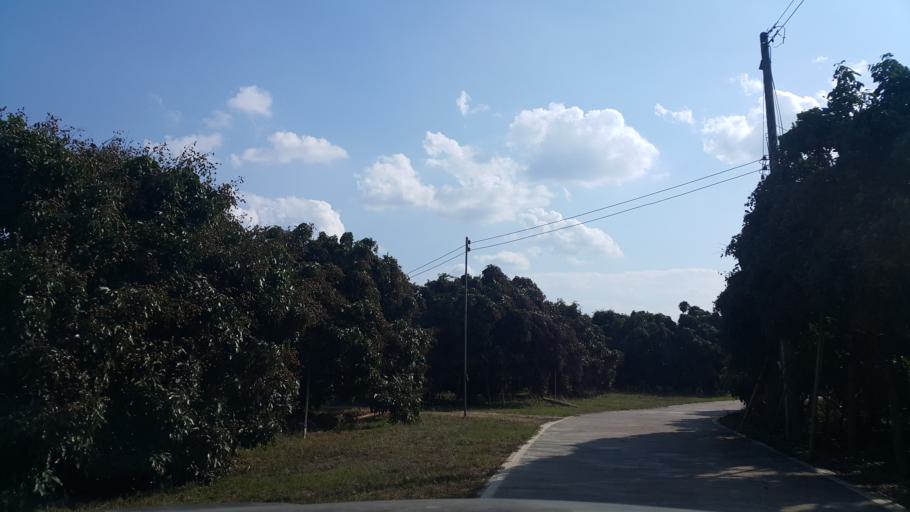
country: TH
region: Lamphun
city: Ban Thi
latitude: 18.5712
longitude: 99.1270
